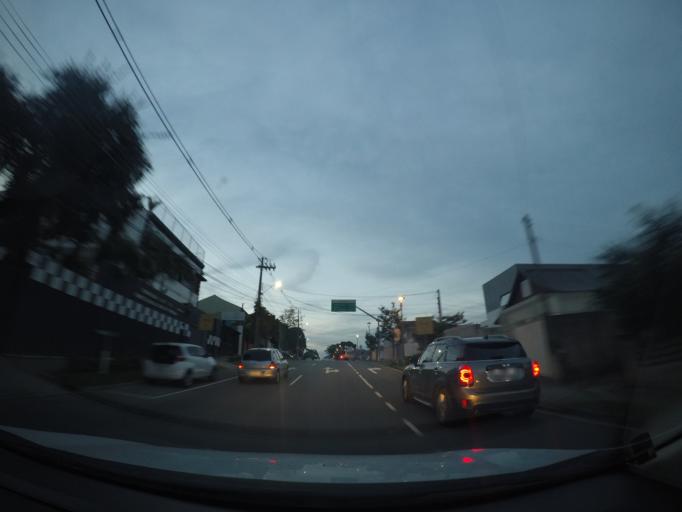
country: BR
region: Parana
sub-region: Curitiba
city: Curitiba
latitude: -25.4158
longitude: -49.2859
